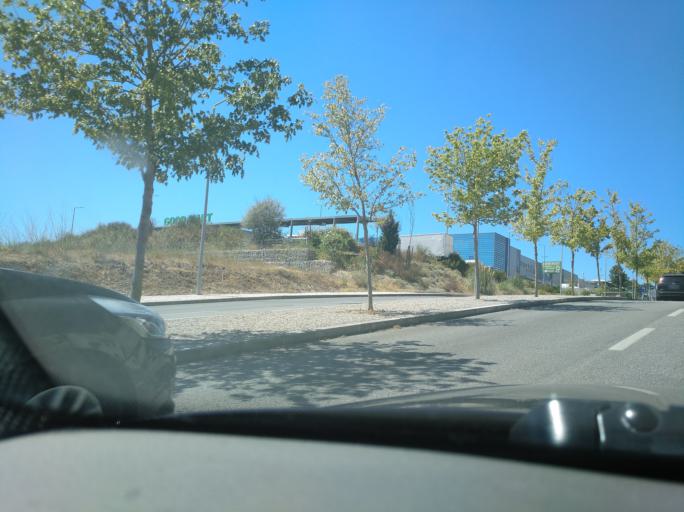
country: PT
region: Lisbon
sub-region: Odivelas
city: Ramada
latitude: 38.7936
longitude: -9.1949
